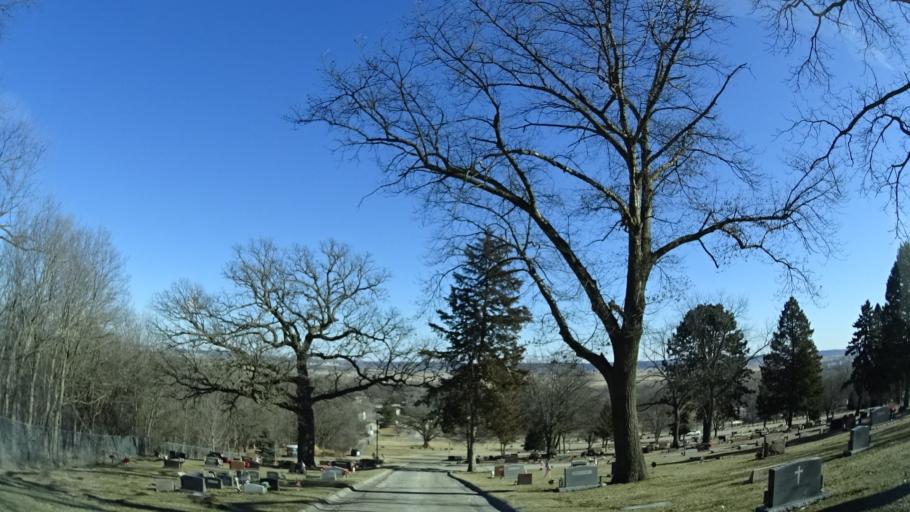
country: US
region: Nebraska
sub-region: Sarpy County
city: Bellevue
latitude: 41.1501
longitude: -95.8945
